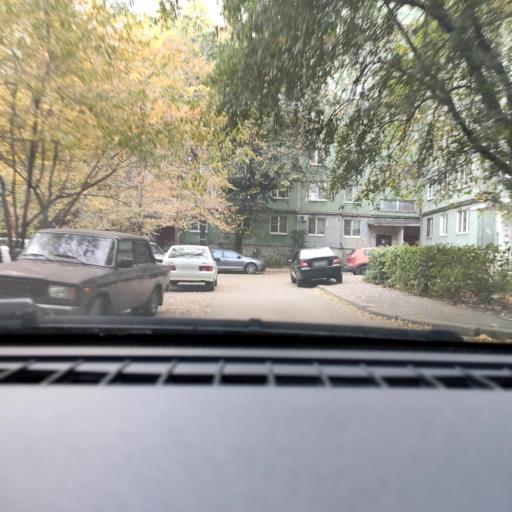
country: RU
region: Voronezj
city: Voronezh
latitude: 51.6864
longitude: 39.1964
